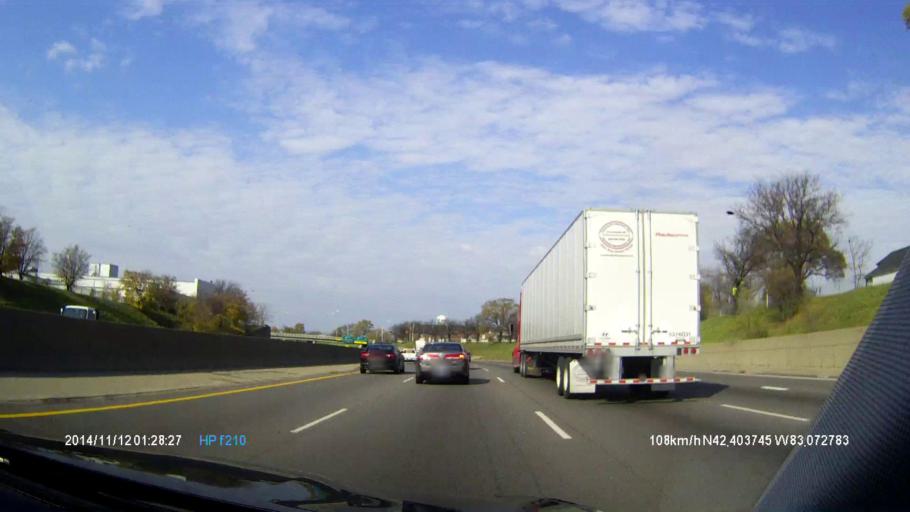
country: US
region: Michigan
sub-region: Wayne County
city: Highland Park
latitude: 42.4042
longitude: -83.0731
